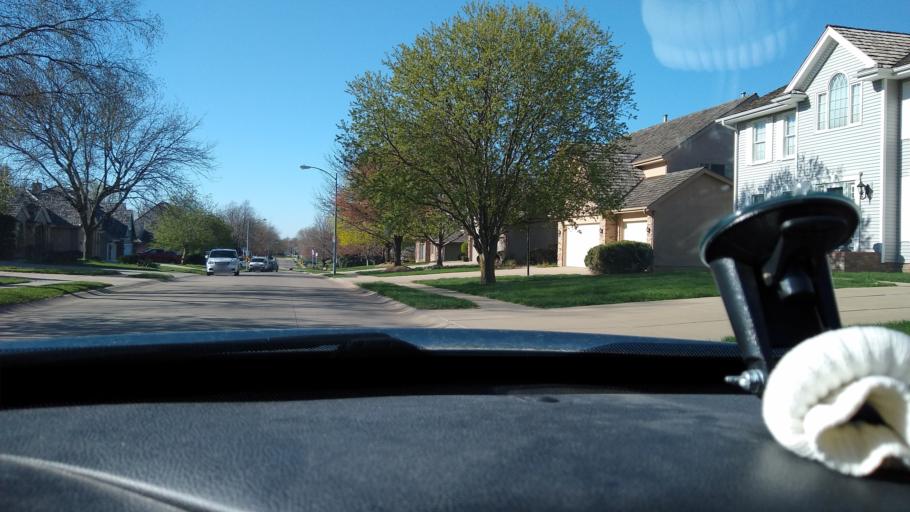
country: US
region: Nebraska
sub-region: Douglas County
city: Ralston
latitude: 41.1957
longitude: -96.0723
